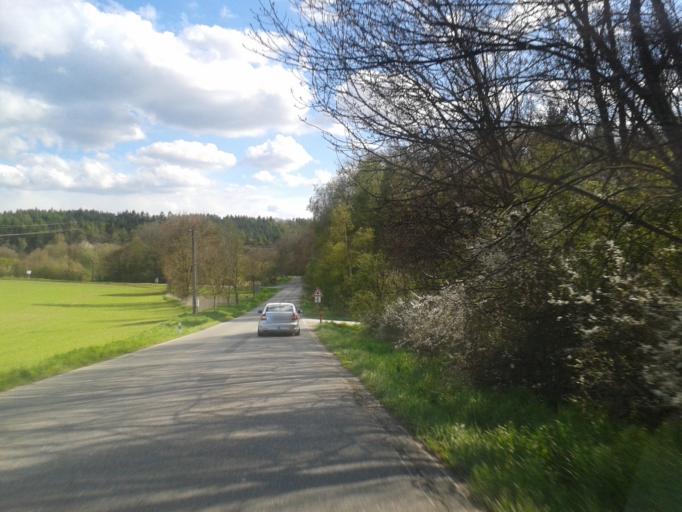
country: CZ
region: Central Bohemia
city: Chynava
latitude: 49.9976
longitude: 14.0922
